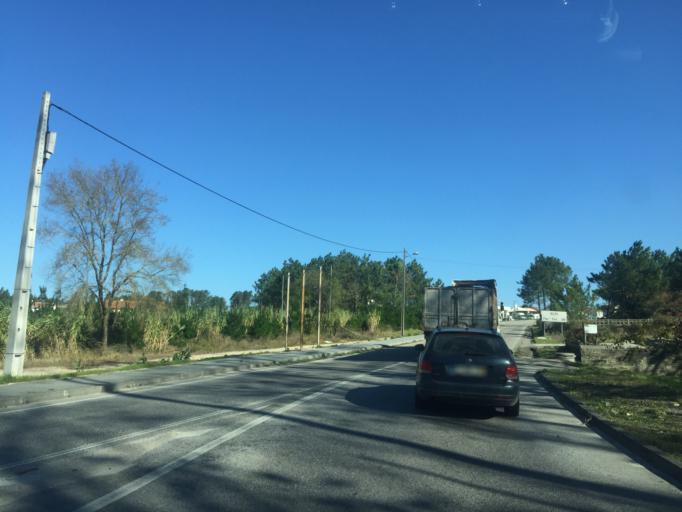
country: PT
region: Leiria
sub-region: Leiria
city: Monte Redondo
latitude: 39.9412
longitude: -8.7939
